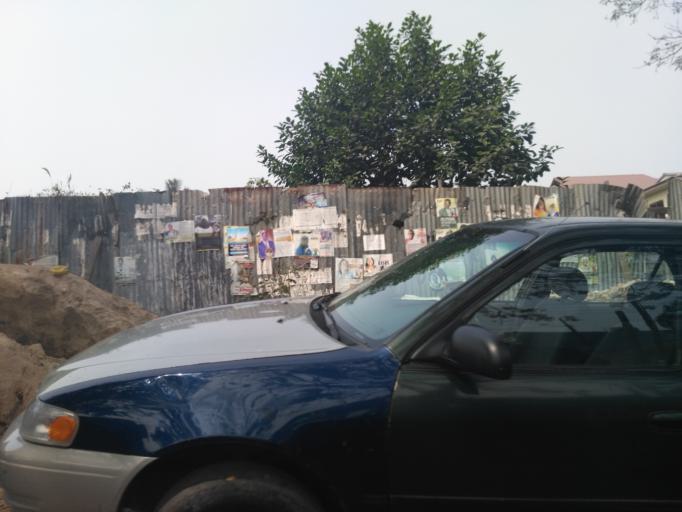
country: GH
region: Ashanti
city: Kumasi
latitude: 6.6796
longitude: -1.6034
